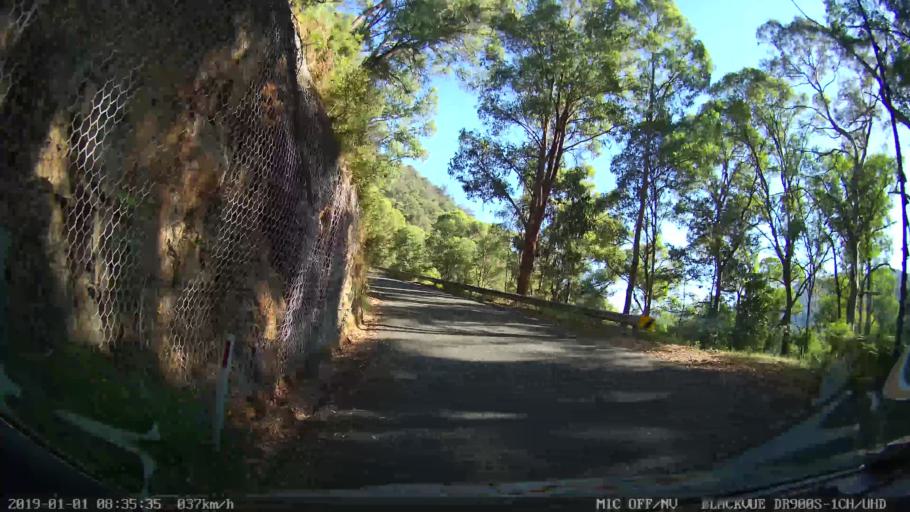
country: AU
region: New South Wales
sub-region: Snowy River
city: Jindabyne
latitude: -36.3484
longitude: 148.1939
